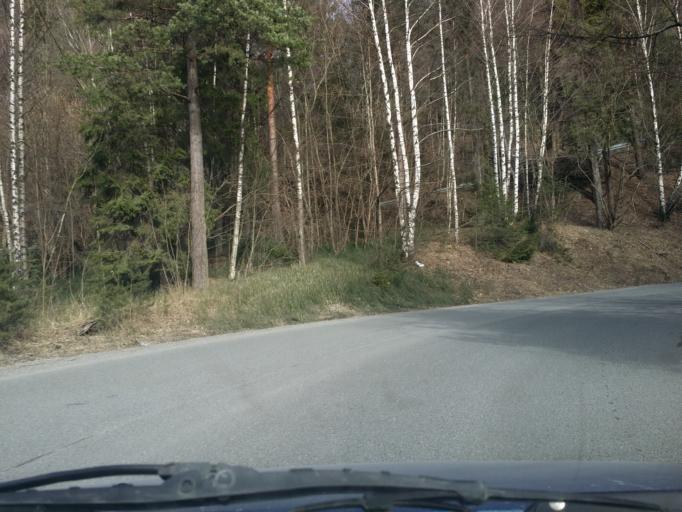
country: NO
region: Buskerud
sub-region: Nedre Eiker
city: Mjondalen
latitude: 59.7588
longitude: 10.0320
